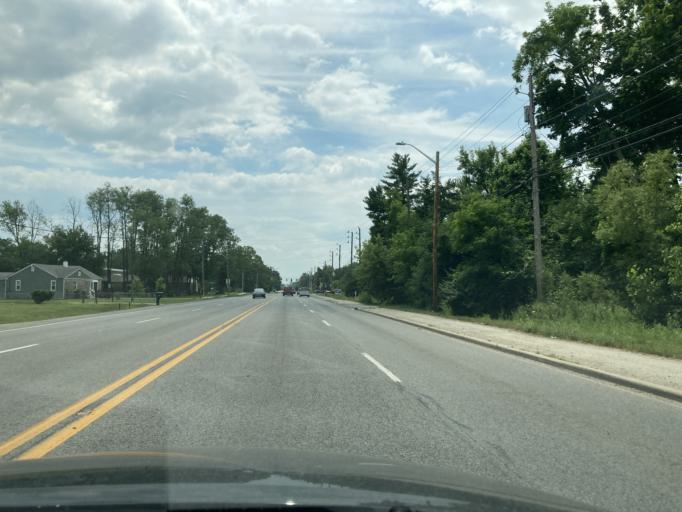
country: US
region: Indiana
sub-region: Marion County
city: Meridian Hills
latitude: 39.8701
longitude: -86.2028
